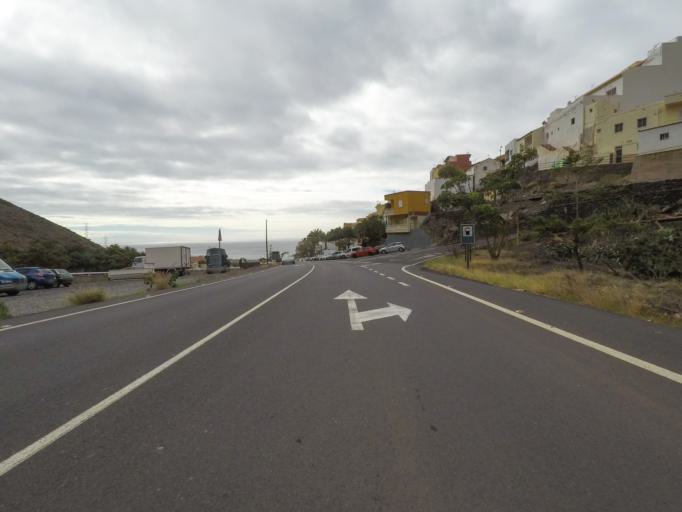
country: ES
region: Canary Islands
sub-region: Provincia de Santa Cruz de Tenerife
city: Alajero
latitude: 28.0967
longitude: -17.3332
